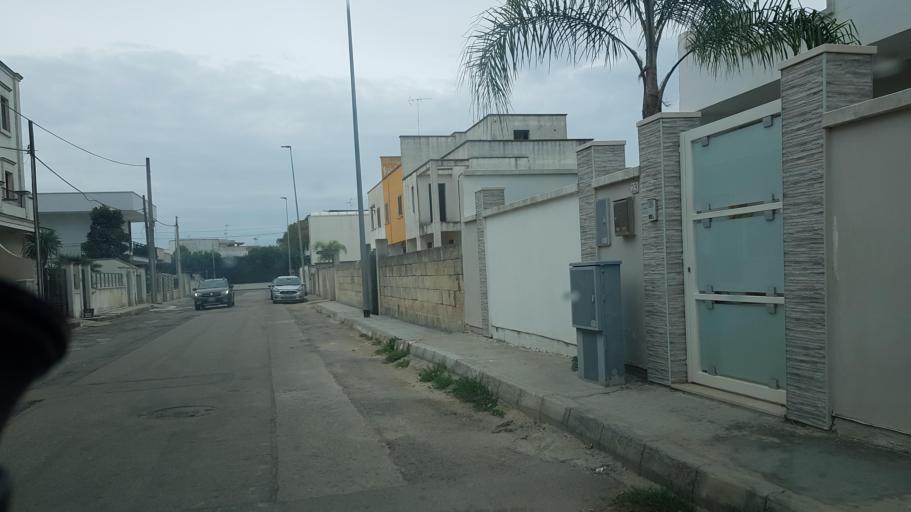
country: IT
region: Apulia
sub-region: Provincia di Lecce
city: Leverano
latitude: 40.2899
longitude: 18.0056
